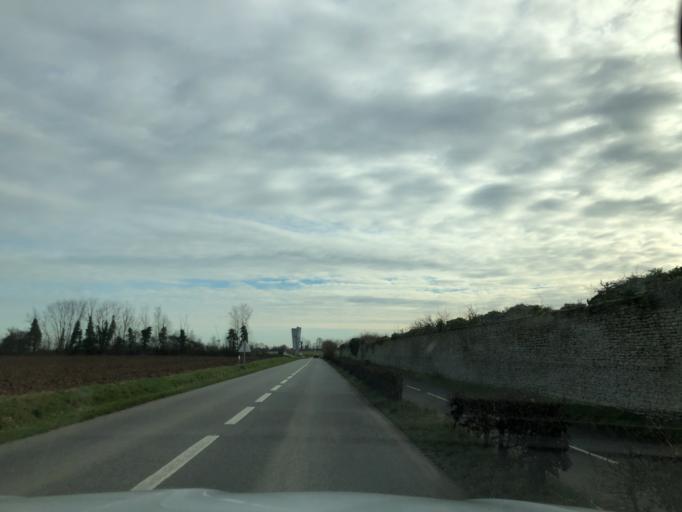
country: FR
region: Lower Normandy
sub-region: Departement du Calvados
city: Beuville
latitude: 49.2405
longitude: -0.3189
